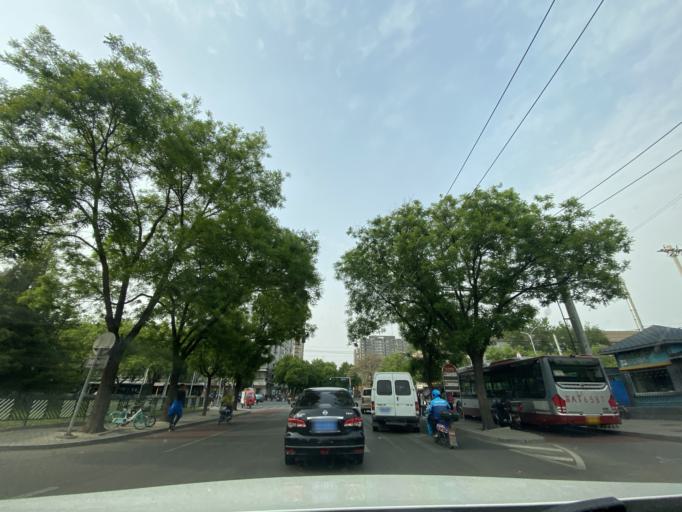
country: CN
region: Beijing
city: Datun
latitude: 39.9747
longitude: 116.3595
